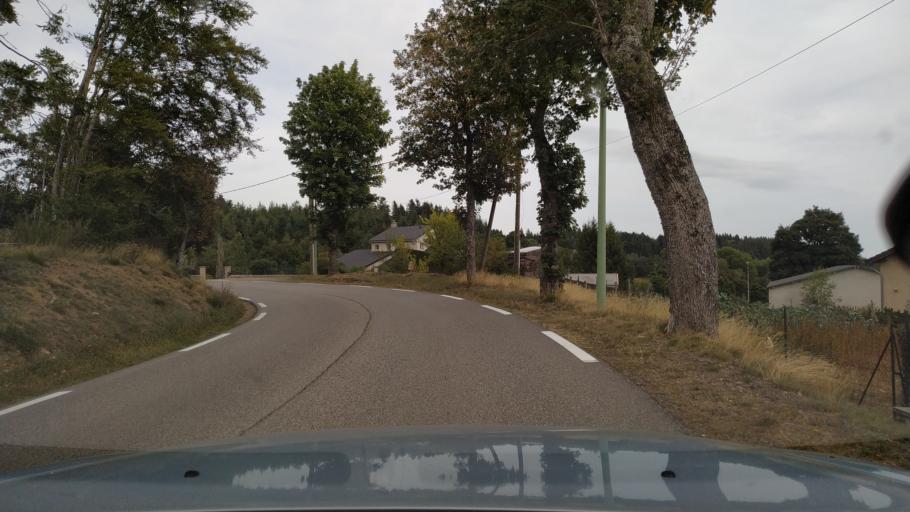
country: FR
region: Rhone-Alpes
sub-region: Departement de l'Ardeche
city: Saint-Agreve
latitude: 45.0127
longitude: 4.4036
